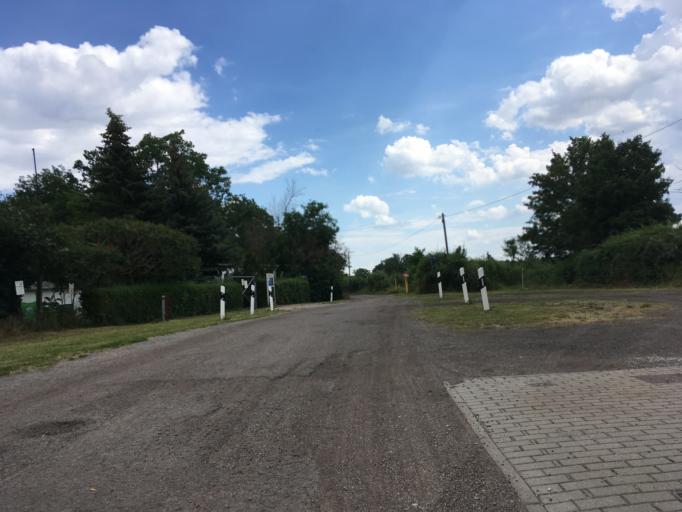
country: DE
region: Saxony-Anhalt
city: Bernburg
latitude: 51.7924
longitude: 11.7625
